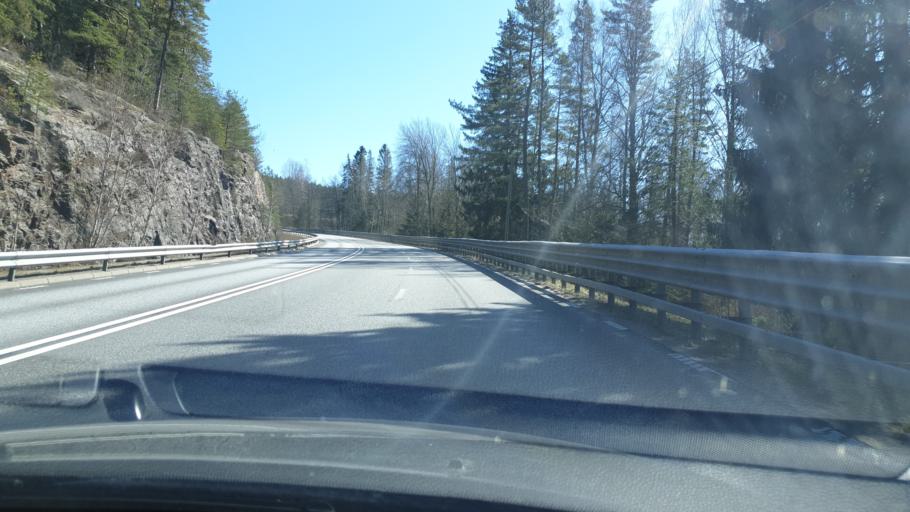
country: SE
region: Vaestra Goetaland
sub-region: Tanums Kommun
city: Tanumshede
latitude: 58.7947
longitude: 11.5733
